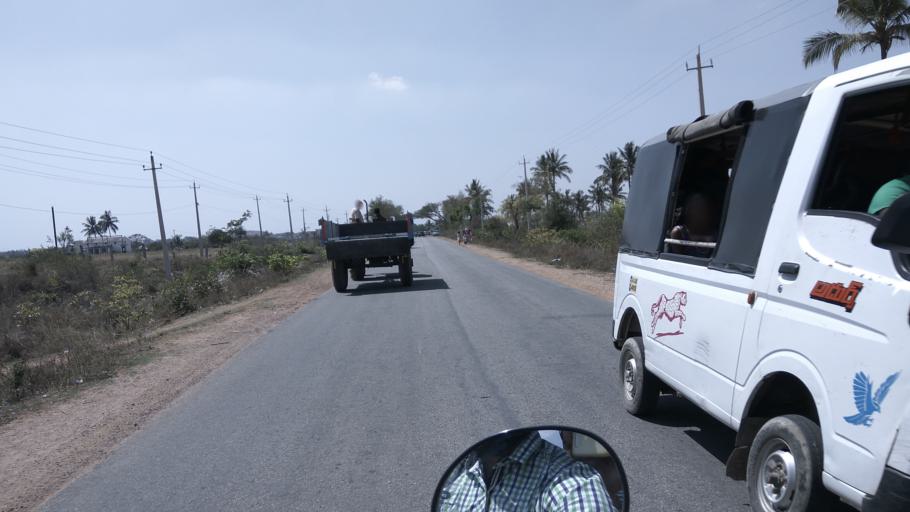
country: IN
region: Karnataka
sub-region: Kolar
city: Mulbagal
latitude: 13.1656
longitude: 78.3691
